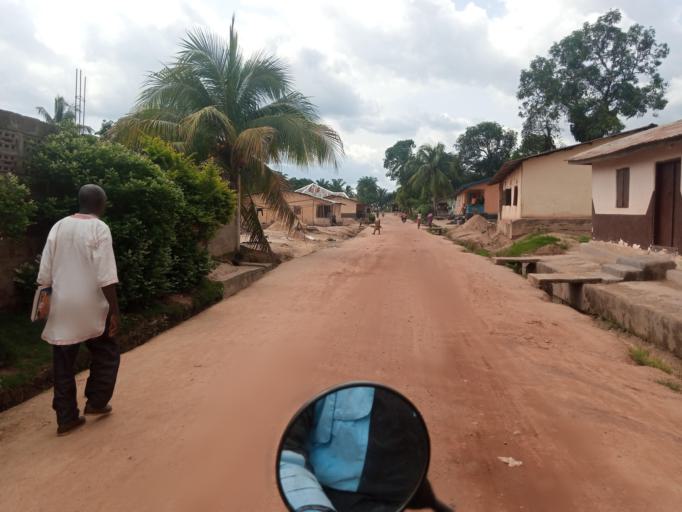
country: SL
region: Southern Province
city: Bo
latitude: 7.9800
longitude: -11.7320
